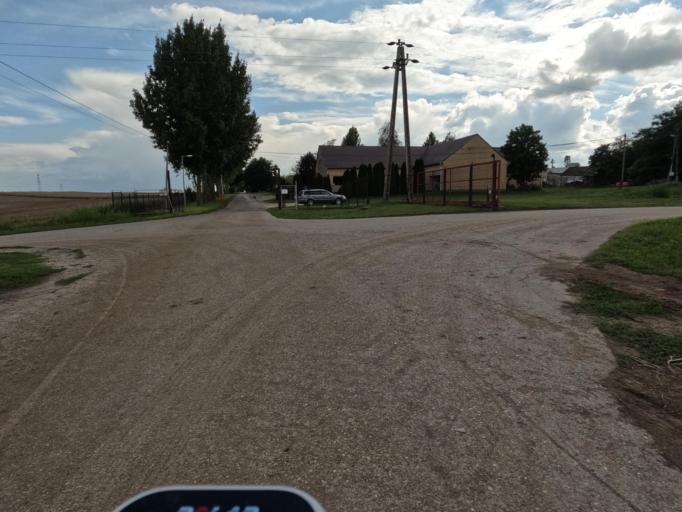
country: HU
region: Tolna
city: Tengelic
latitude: 46.5207
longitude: 18.7059
